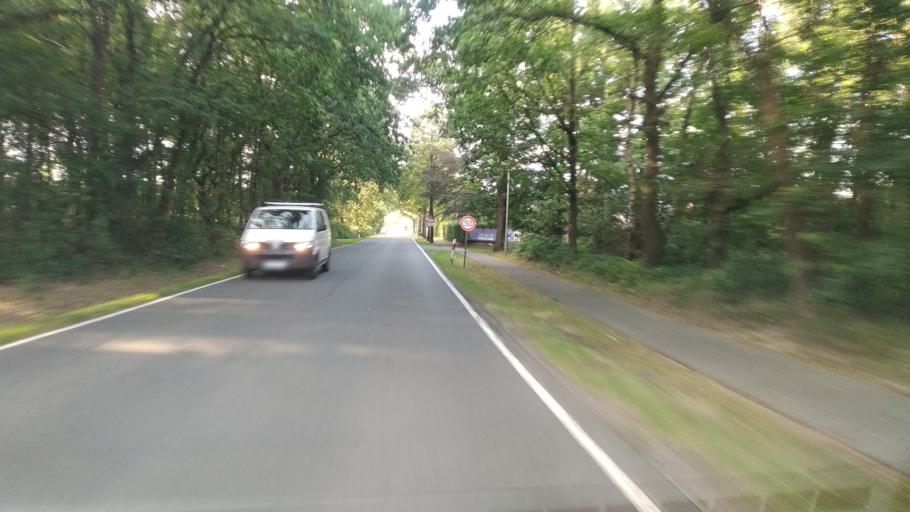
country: DE
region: Schleswig-Holstein
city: Kropp
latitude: 54.4042
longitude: 9.5113
